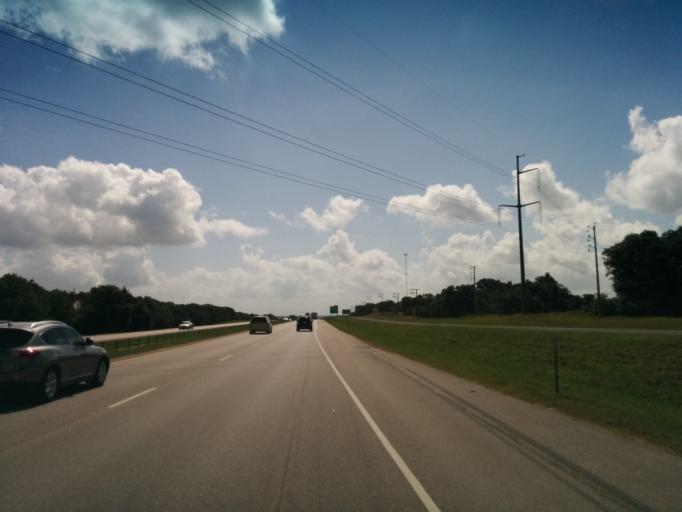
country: US
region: Texas
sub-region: Colorado County
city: Columbus
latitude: 29.6933
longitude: -96.6058
